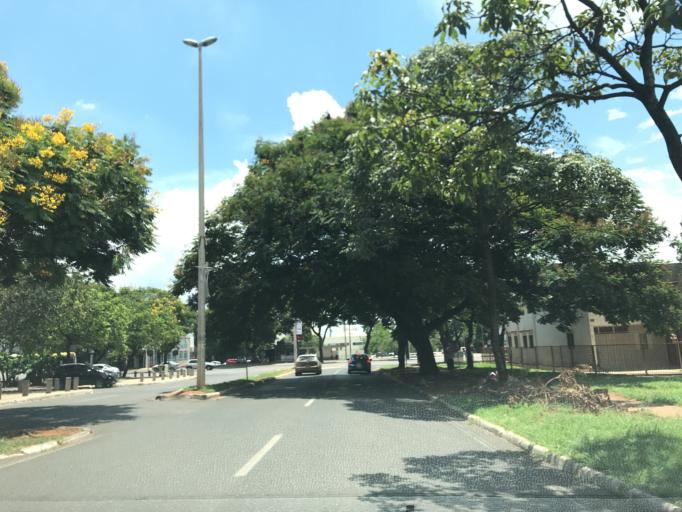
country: BR
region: Federal District
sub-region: Brasilia
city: Brasilia
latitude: -15.8010
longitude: -47.8952
